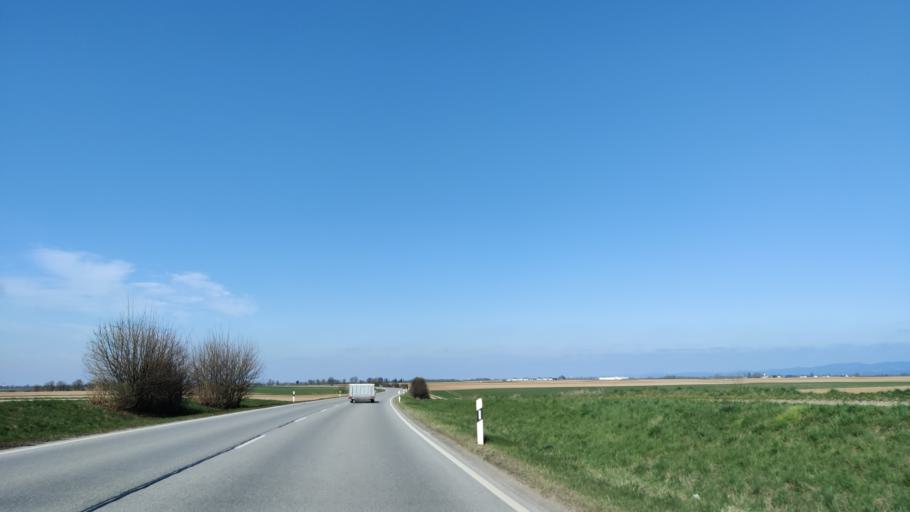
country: DE
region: Bavaria
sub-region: Lower Bavaria
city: Strasskirchen
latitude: 48.8402
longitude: 12.6776
